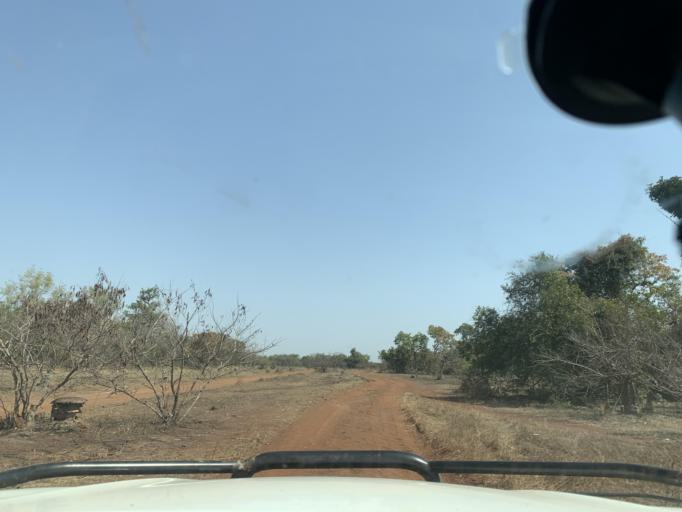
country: ML
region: Sikasso
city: Kolondieba
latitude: 10.8884
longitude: -6.7588
